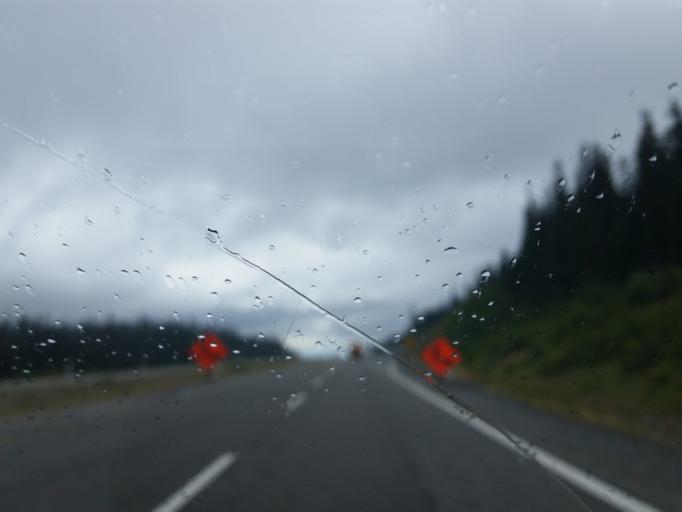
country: CA
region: British Columbia
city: Peachland
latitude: 49.9067
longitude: -120.0129
